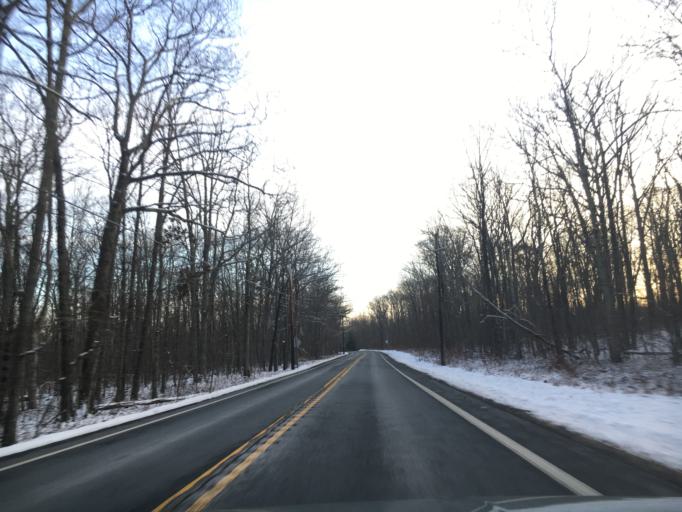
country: US
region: Pennsylvania
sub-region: Pike County
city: Saw Creek
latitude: 41.2218
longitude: -75.0809
